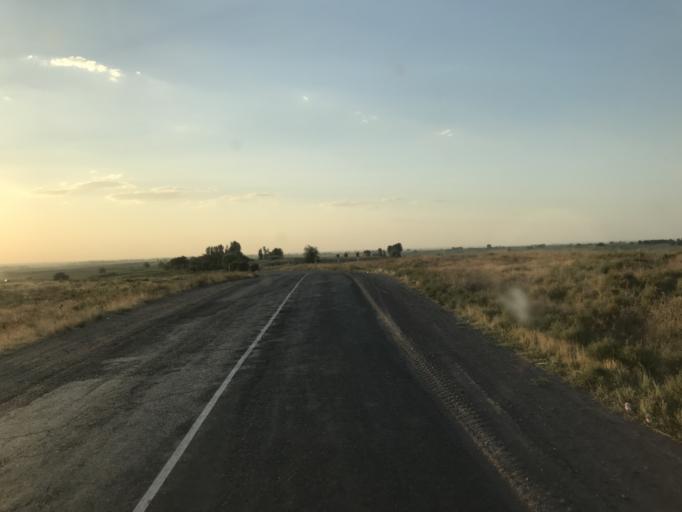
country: UZ
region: Toshkent
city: Yangiyul
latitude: 41.3448
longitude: 68.8758
